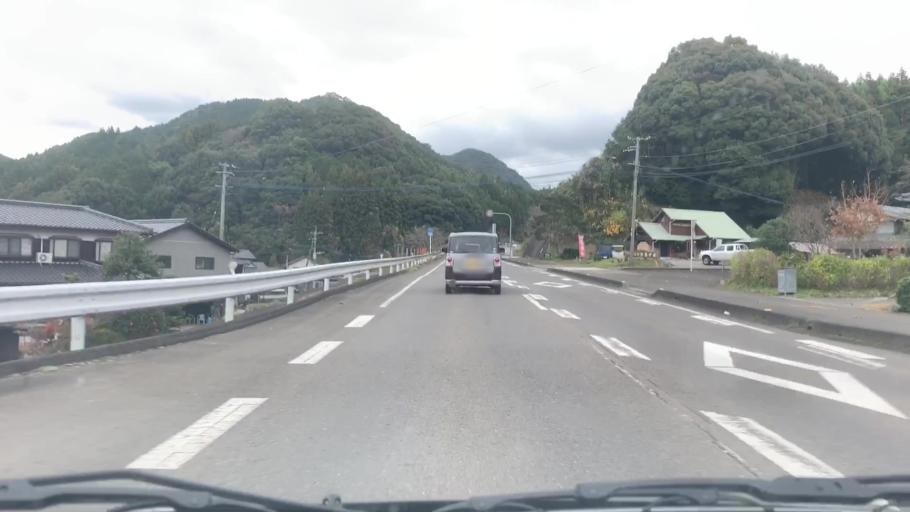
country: JP
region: Saga Prefecture
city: Ureshinomachi-shimojuku
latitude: 33.0924
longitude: 130.0276
